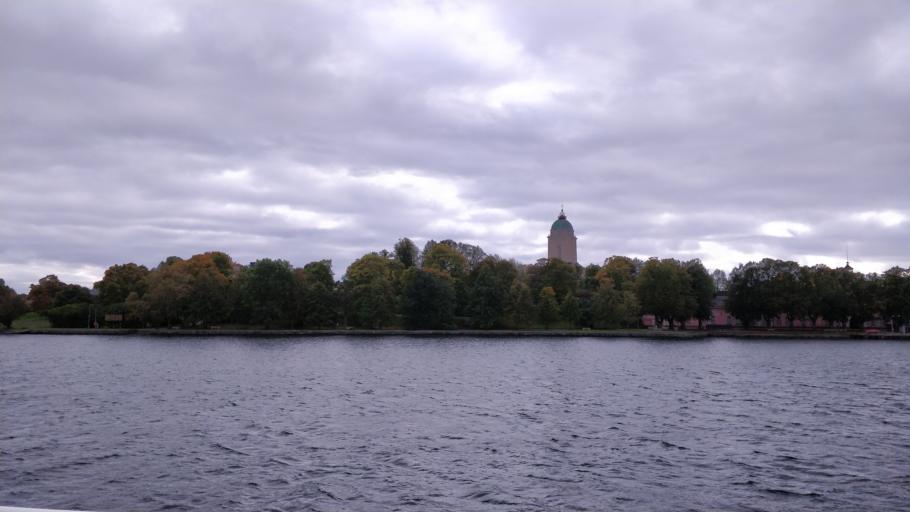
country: FI
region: Uusimaa
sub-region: Helsinki
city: Helsinki
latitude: 60.1509
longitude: 24.9879
